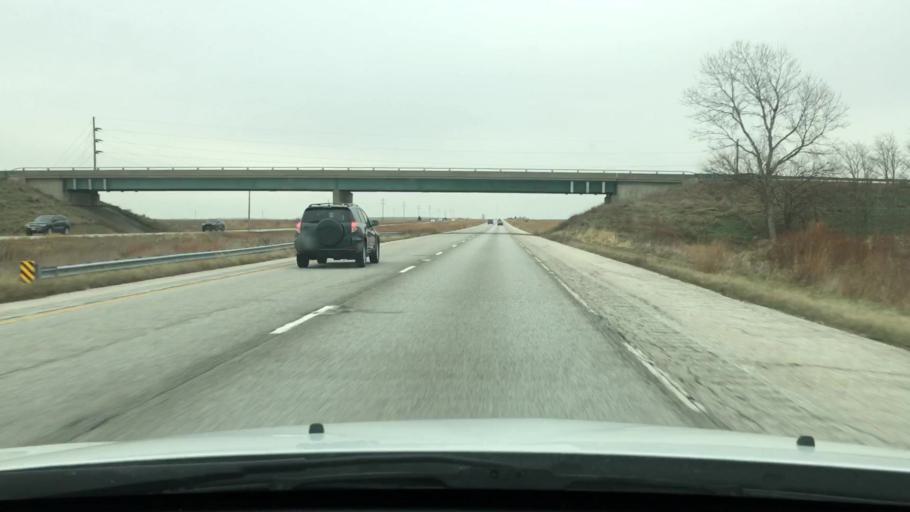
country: US
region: Illinois
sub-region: Morgan County
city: Jacksonville
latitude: 39.7378
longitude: -90.1275
